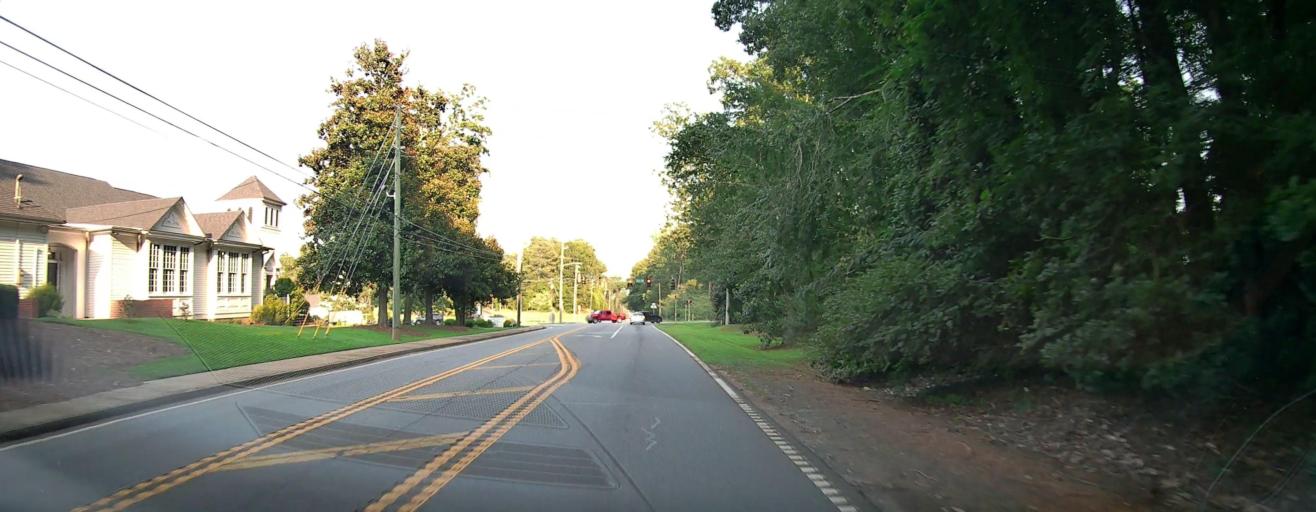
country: US
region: Georgia
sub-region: Bibb County
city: West Point
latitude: 32.8897
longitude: -83.7470
